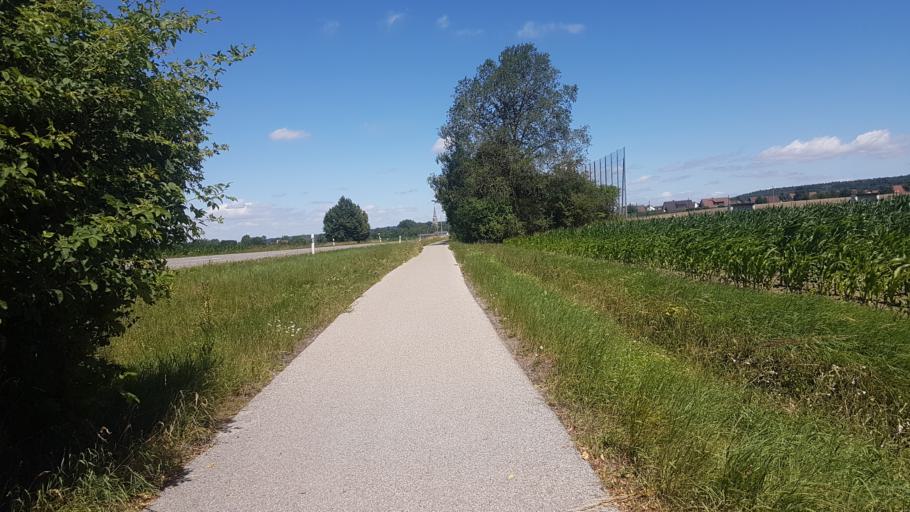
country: DE
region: Bavaria
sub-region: Regierungsbezirk Mittelfranken
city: Herrieden
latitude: 49.2533
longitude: 10.4636
